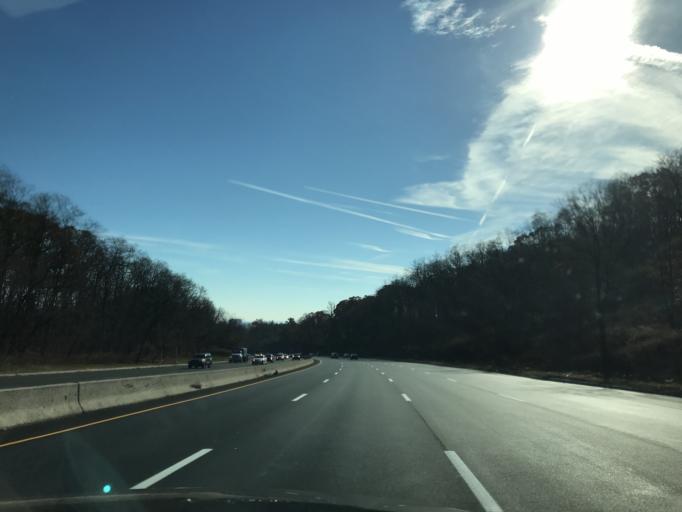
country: US
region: New Jersey
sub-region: Essex County
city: West Orange
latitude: 40.7901
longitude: -74.2492
